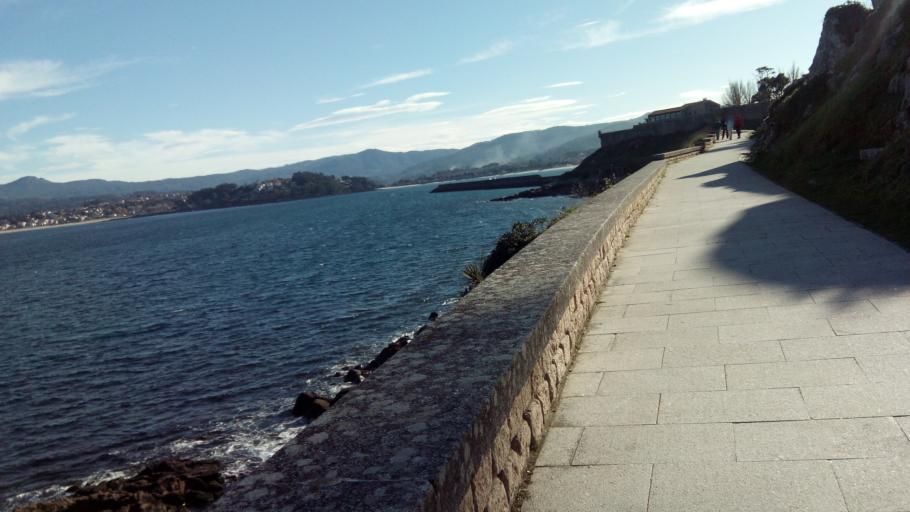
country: ES
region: Galicia
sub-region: Provincia de Pontevedra
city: Baiona
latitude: 42.1279
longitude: -8.8512
